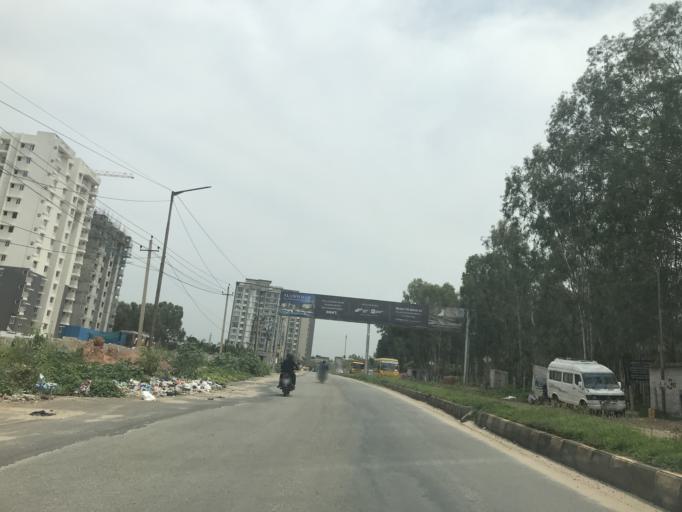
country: IN
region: Karnataka
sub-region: Bangalore Urban
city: Yelahanka
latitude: 13.0861
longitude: 77.6545
